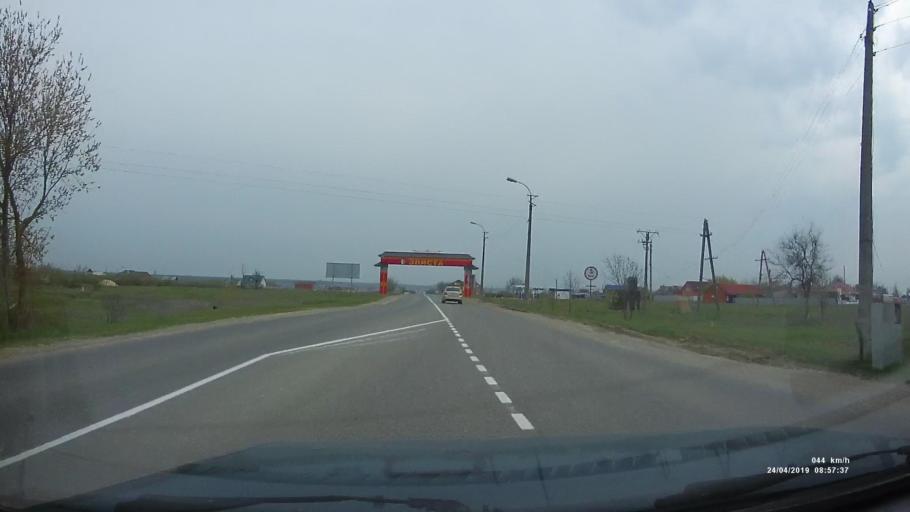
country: RU
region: Kalmykiya
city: Arshan'
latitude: 46.3036
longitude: 44.1892
